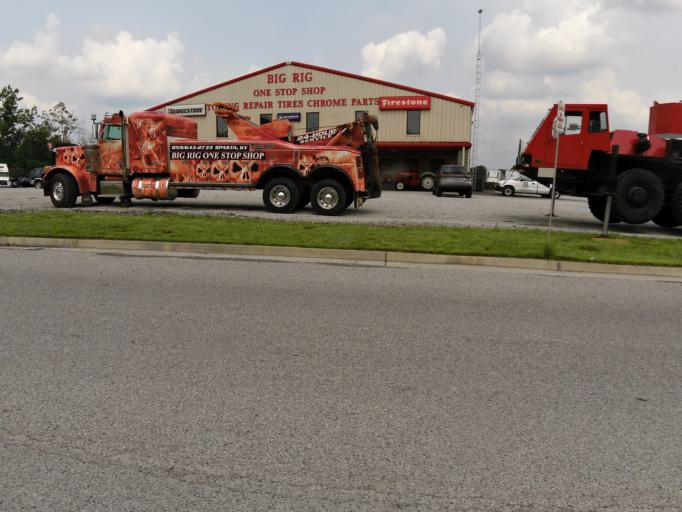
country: US
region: Kentucky
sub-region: Gallatin County
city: Warsaw
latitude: 38.6944
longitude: -84.9397
